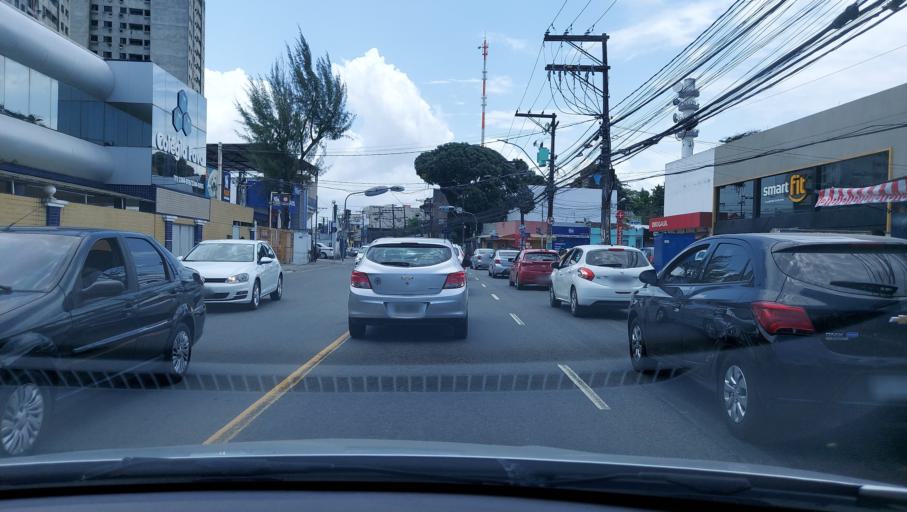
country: BR
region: Bahia
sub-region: Salvador
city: Salvador
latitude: -12.9607
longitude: -38.4680
